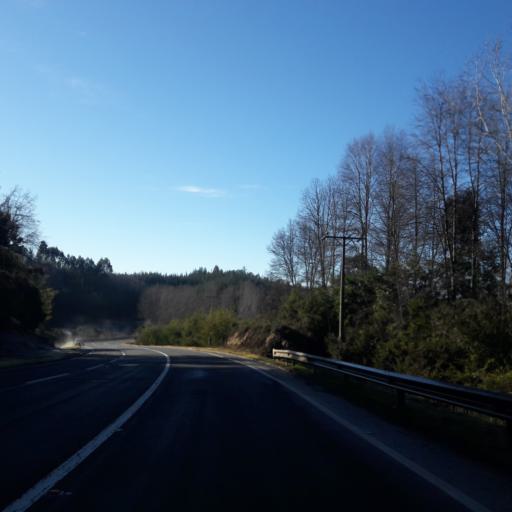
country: CL
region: Biobio
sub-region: Provincia de Biobio
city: La Laja
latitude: -37.2732
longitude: -72.9547
